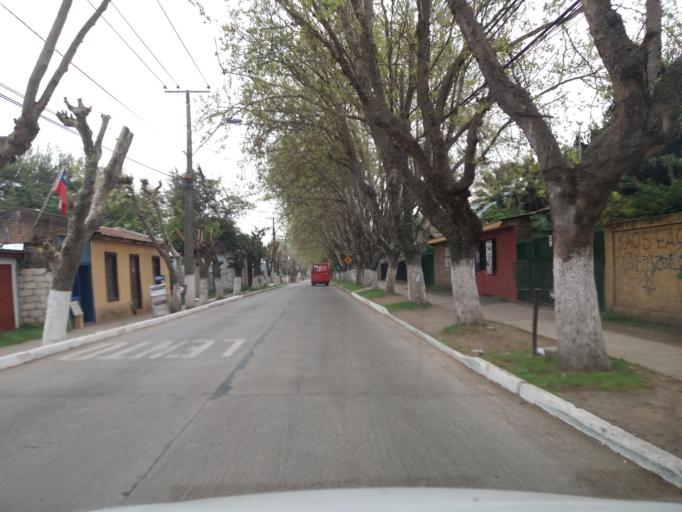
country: CL
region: Valparaiso
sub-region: Provincia de Quillota
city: Hacienda La Calera
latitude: -32.7994
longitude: -71.1460
